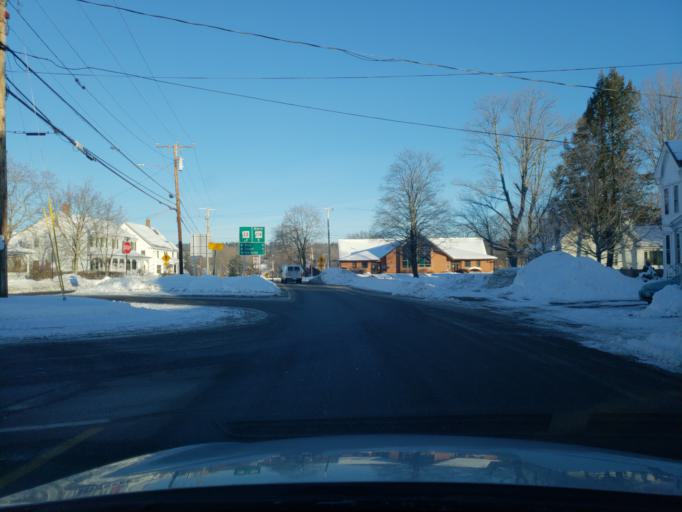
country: US
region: New Hampshire
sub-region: Hillsborough County
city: Goffstown
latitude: 43.0163
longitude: -71.5980
